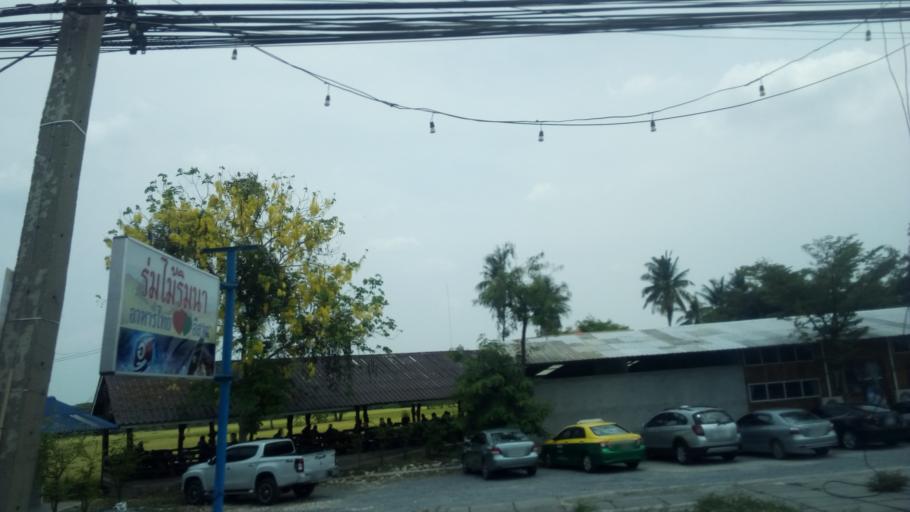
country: TH
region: Nakhon Pathom
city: Salaya
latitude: 13.7841
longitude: 100.3027
